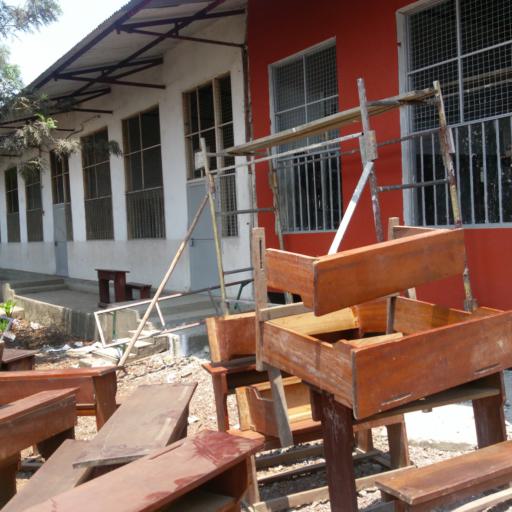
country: CD
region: Nord Kivu
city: Goma
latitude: -1.6455
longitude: 29.2332
